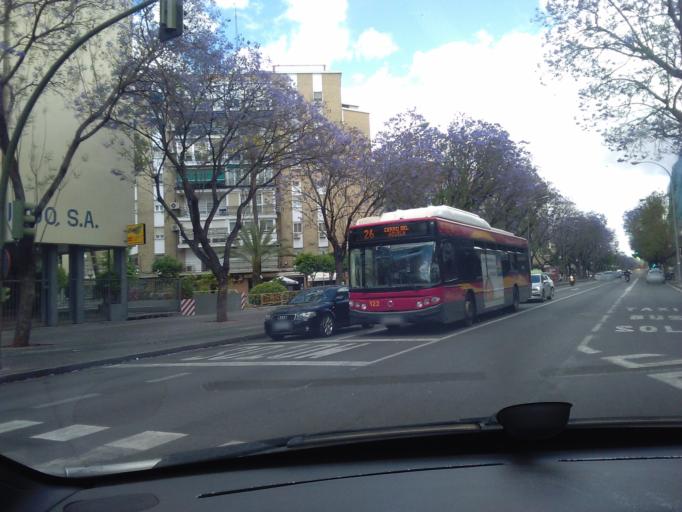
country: ES
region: Andalusia
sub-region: Provincia de Sevilla
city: Sevilla
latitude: 37.3771
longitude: -5.9748
